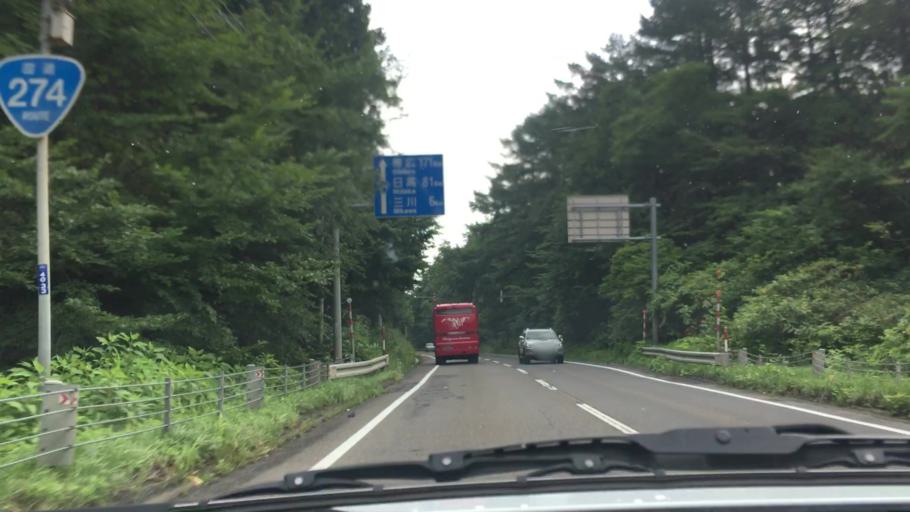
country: JP
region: Hokkaido
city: Chitose
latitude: 42.9438
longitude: 141.7461
